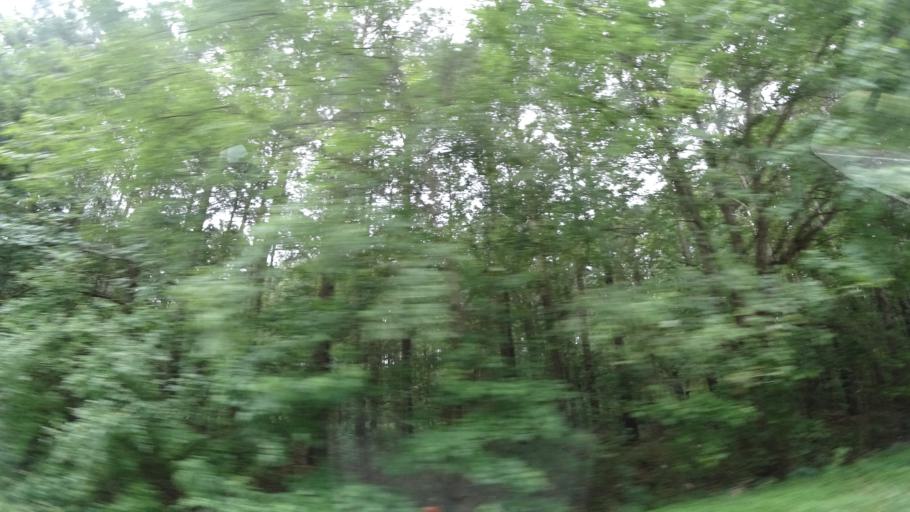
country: US
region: Virginia
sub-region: Spotsylvania County
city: Spotsylvania
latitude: 38.1478
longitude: -77.7048
